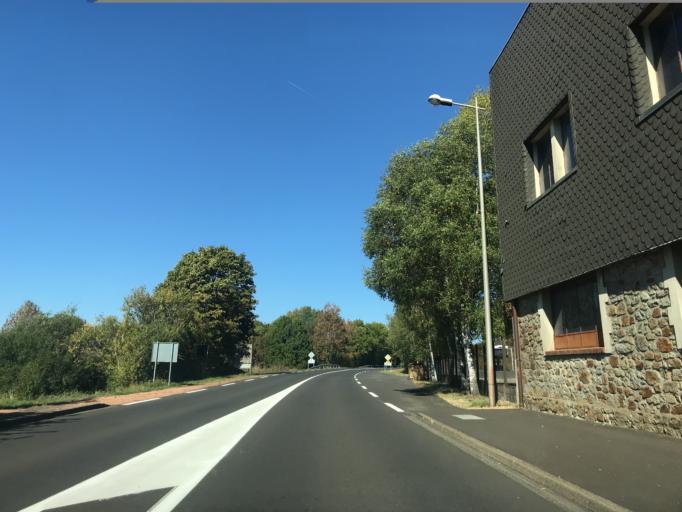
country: FR
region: Auvergne
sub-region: Departement du Puy-de-Dome
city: Gelles
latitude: 45.6920
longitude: 2.8070
